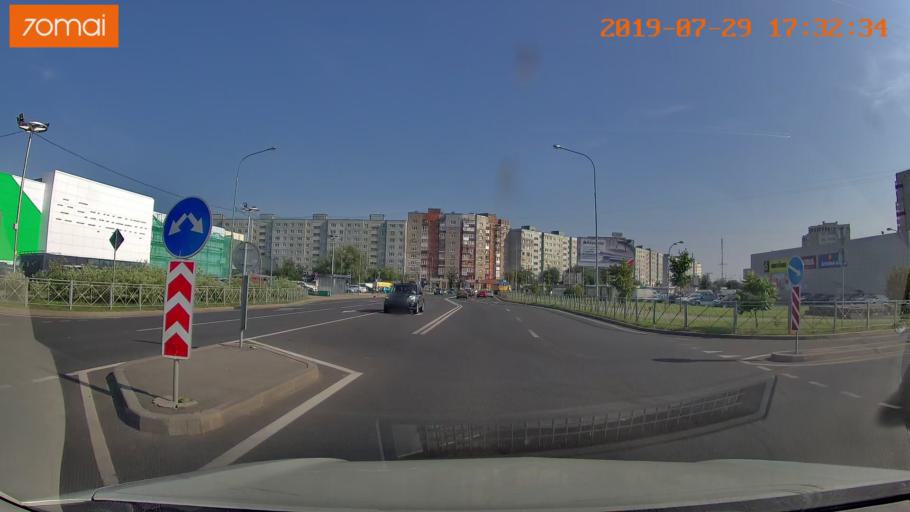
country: RU
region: Kaliningrad
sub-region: Gorod Kaliningrad
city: Kaliningrad
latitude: 54.7414
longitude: 20.4939
